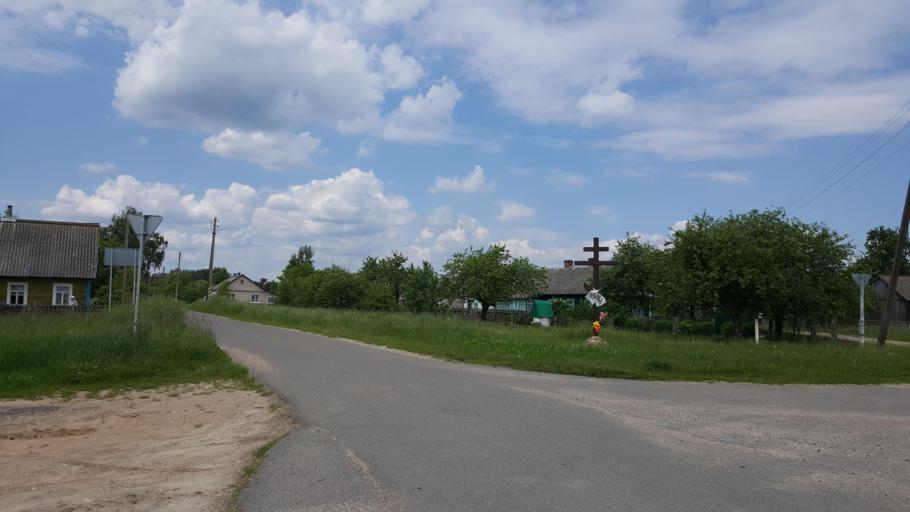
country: PL
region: Podlasie
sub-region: Powiat hajnowski
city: Bialowieza
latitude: 52.6673
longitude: 24.0781
